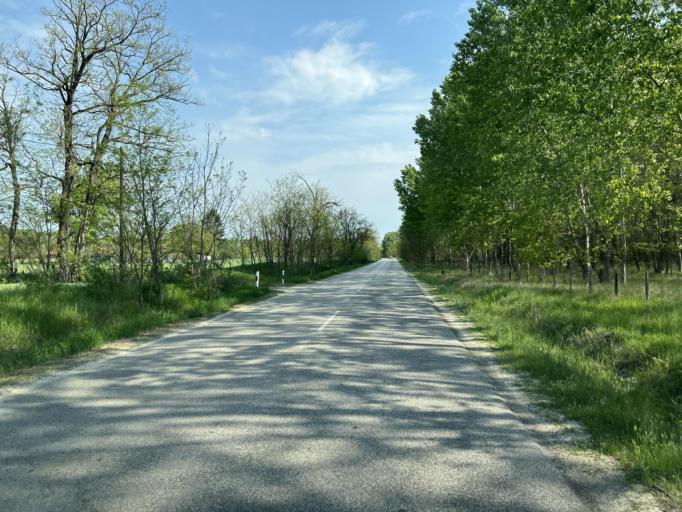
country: HU
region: Pest
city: Kocser
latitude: 47.0189
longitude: 19.9325
